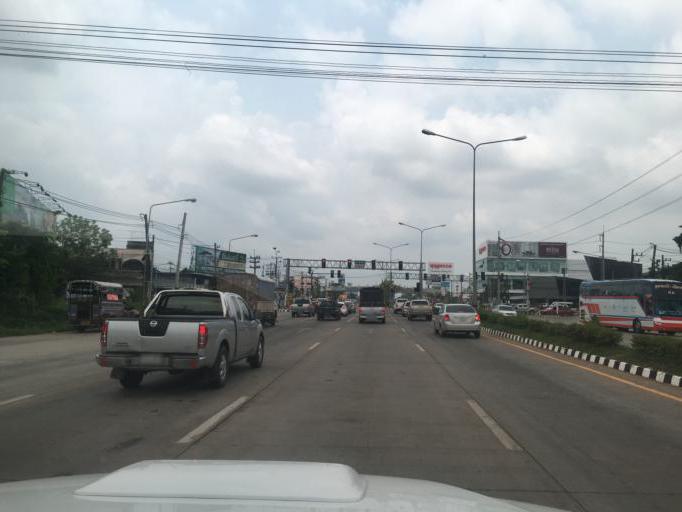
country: TH
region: Changwat Udon Thani
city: Udon Thani
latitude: 17.4079
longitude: 102.7660
